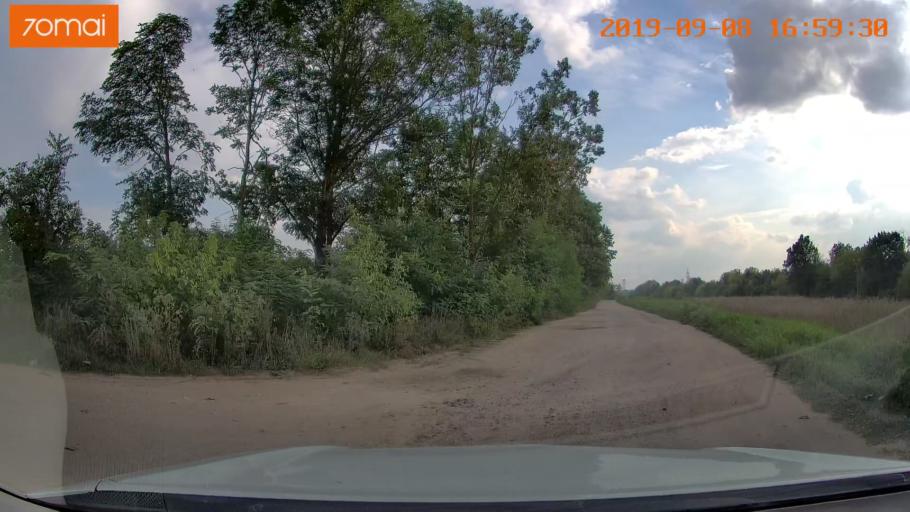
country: BY
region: Grodnenskaya
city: Hrodna
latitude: 53.7232
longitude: 23.9337
